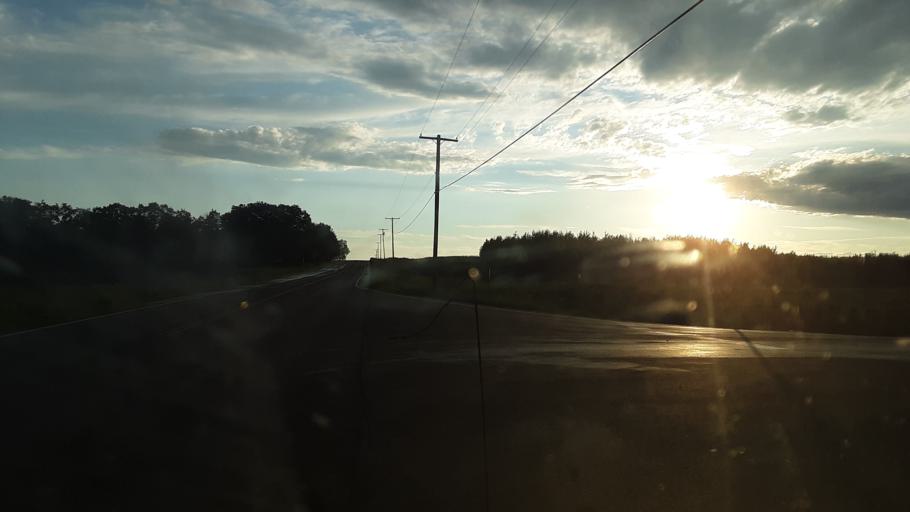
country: US
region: Maine
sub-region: Aroostook County
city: Presque Isle
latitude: 46.6749
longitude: -67.9731
